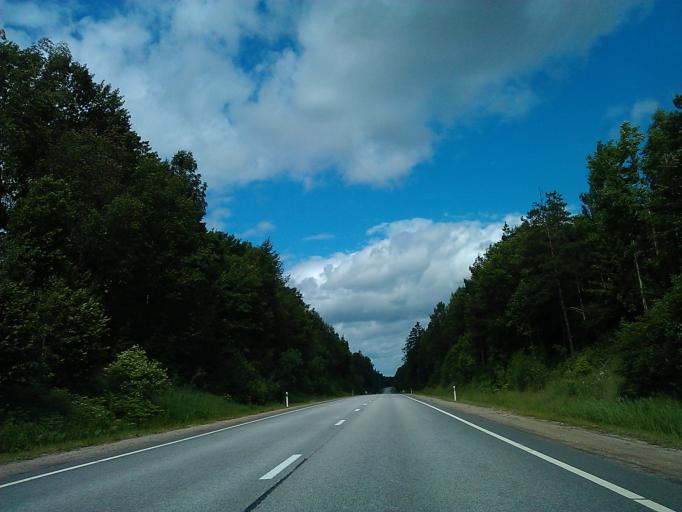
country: LV
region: Tukuma Rajons
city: Tukums
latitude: 56.9906
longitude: 23.0240
